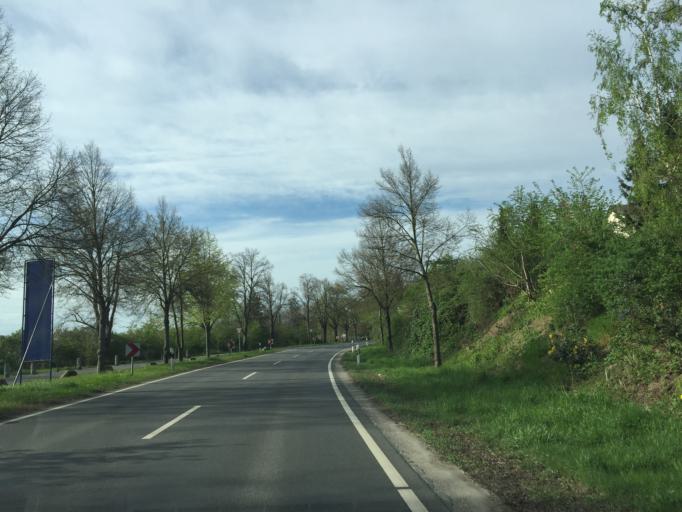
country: DE
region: Hesse
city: Zwingenberg
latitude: 49.7313
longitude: 8.6085
